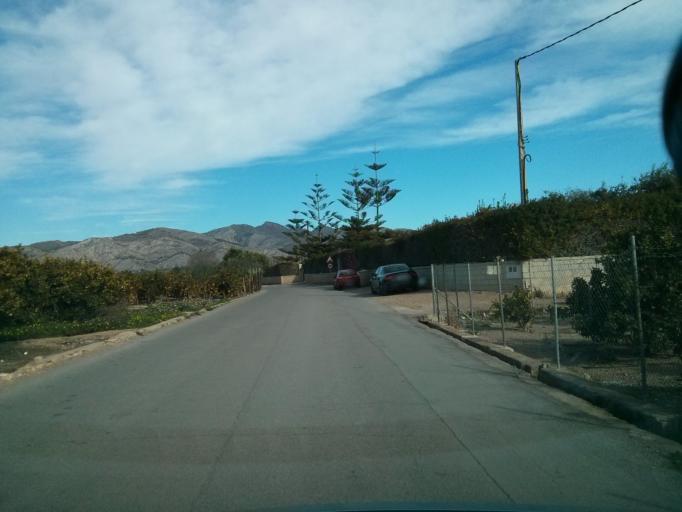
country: ES
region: Valencia
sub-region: Provincia de Castello
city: Castello de la Plana
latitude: 40.0046
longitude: -0.0225
